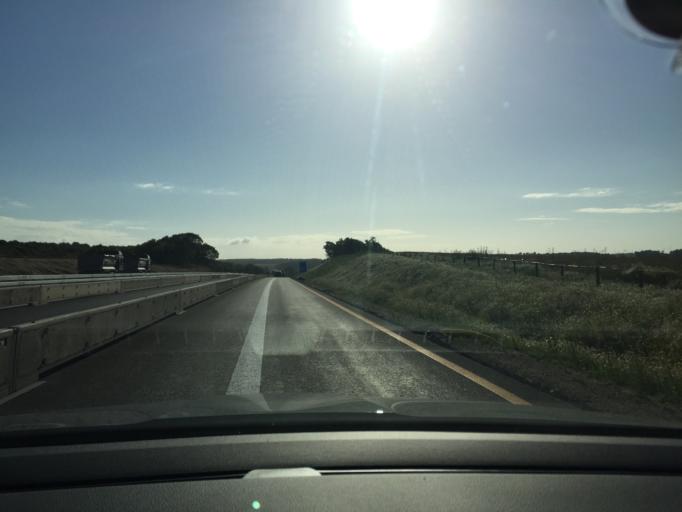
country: DE
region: Brandenburg
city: Brussow
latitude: 53.2921
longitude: 14.1068
